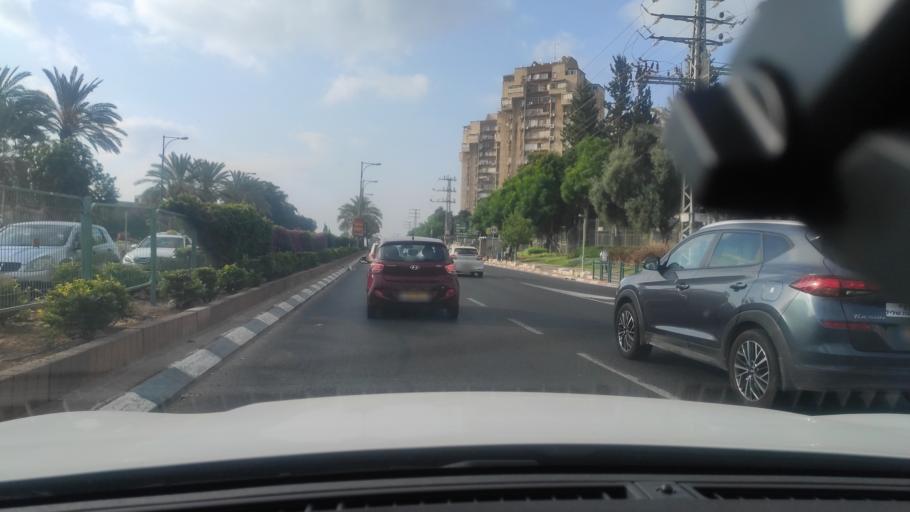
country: IL
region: Central District
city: Petah Tiqwa
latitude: 32.1018
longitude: 34.8980
